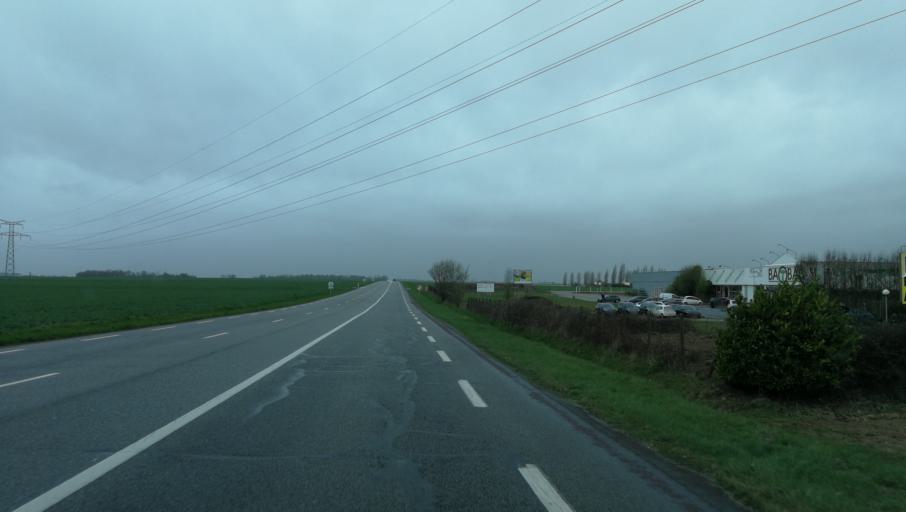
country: FR
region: Haute-Normandie
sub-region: Departement de l'Eure
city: Saint-Sebastien-de-Morsent
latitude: 49.0474
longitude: 1.0718
